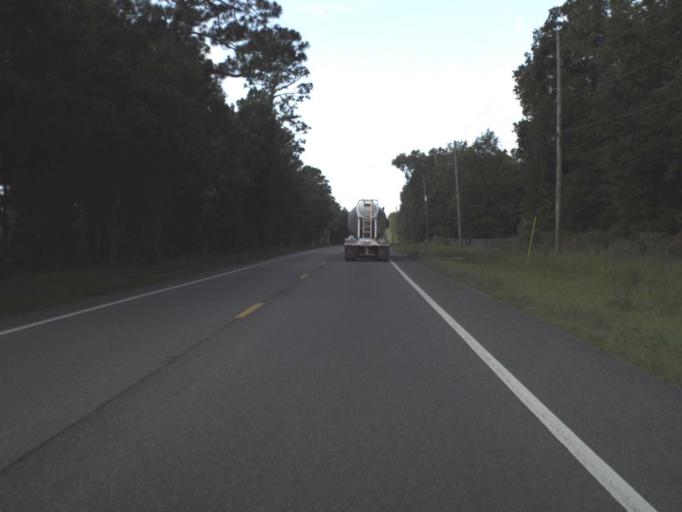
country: US
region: Florida
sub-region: Columbia County
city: Lake City
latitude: 30.1347
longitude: -82.7117
